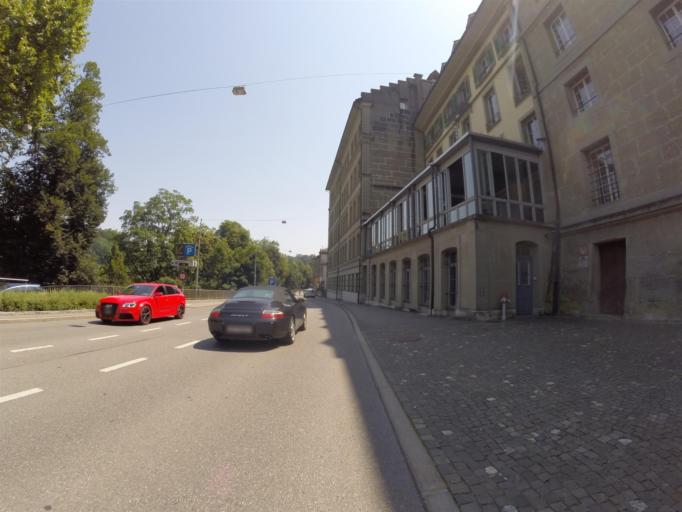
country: CH
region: Bern
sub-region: Bern-Mittelland District
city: Bern
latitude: 46.9489
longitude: 7.4527
